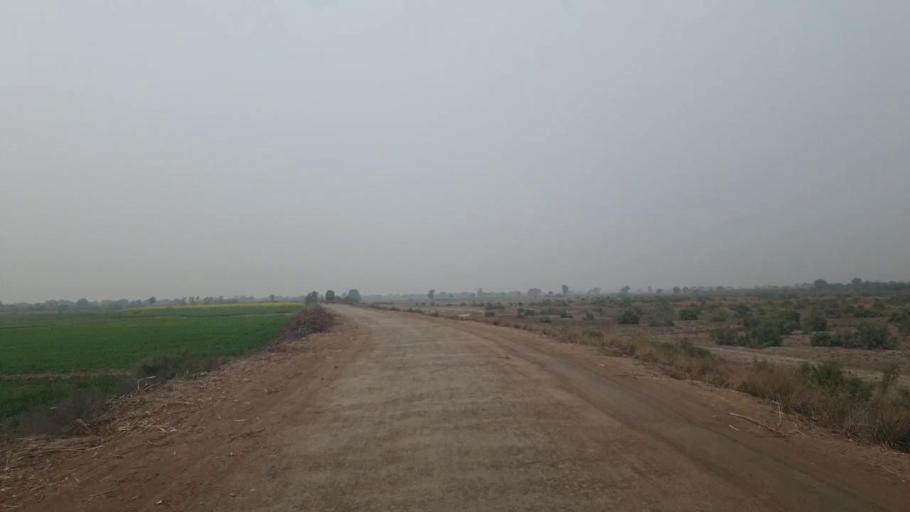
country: PK
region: Sindh
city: Tando Adam
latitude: 25.8061
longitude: 68.7208
